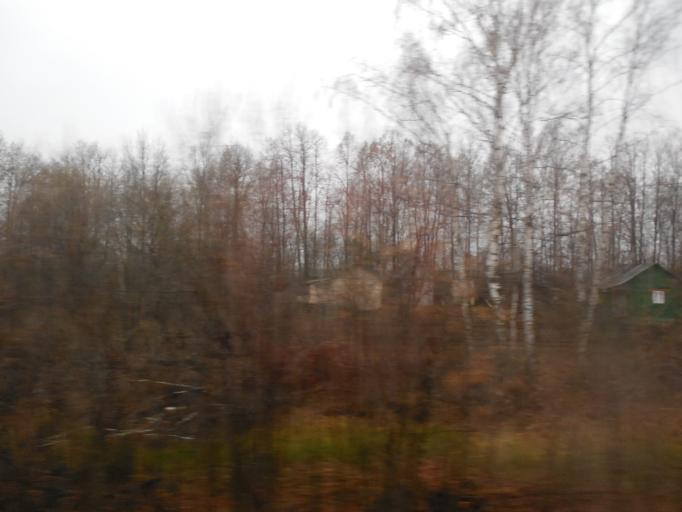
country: RU
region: Moskovskaya
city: Belyye Stolby
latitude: 55.3174
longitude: 37.8651
